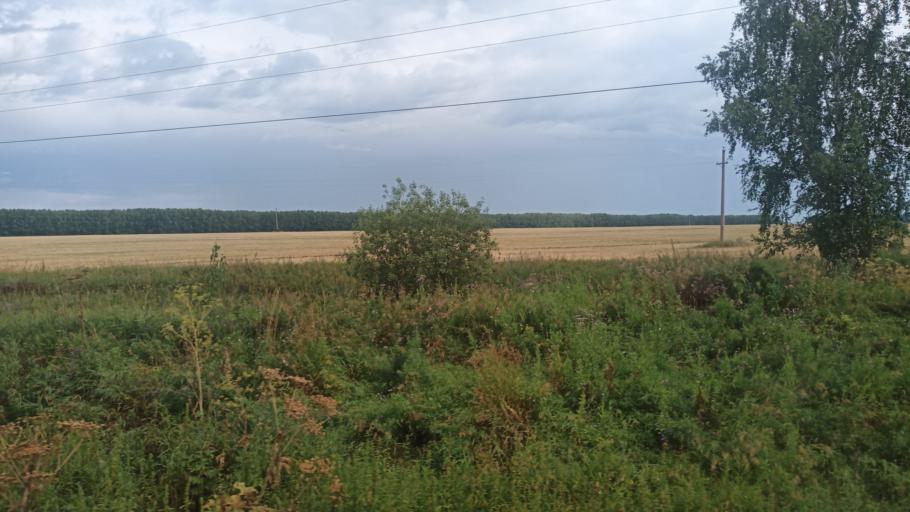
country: RU
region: Altai Krai
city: Nalobikha
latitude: 53.2360
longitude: 84.4665
